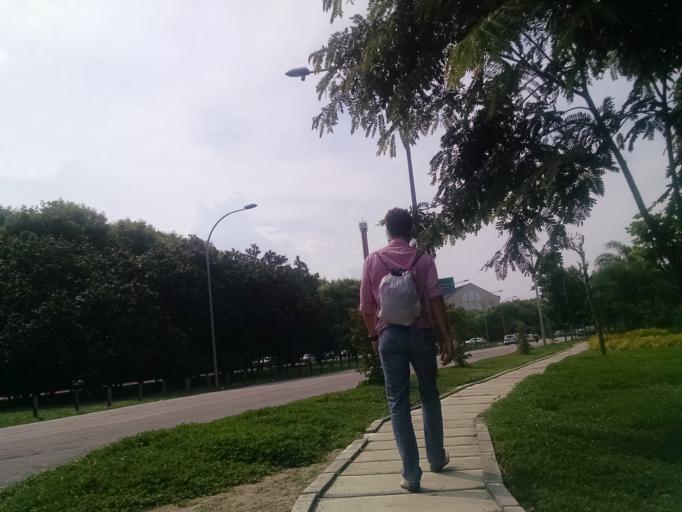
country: BR
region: Rio de Janeiro
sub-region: Rio De Janeiro
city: Rio de Janeiro
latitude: -22.9906
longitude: -43.3608
